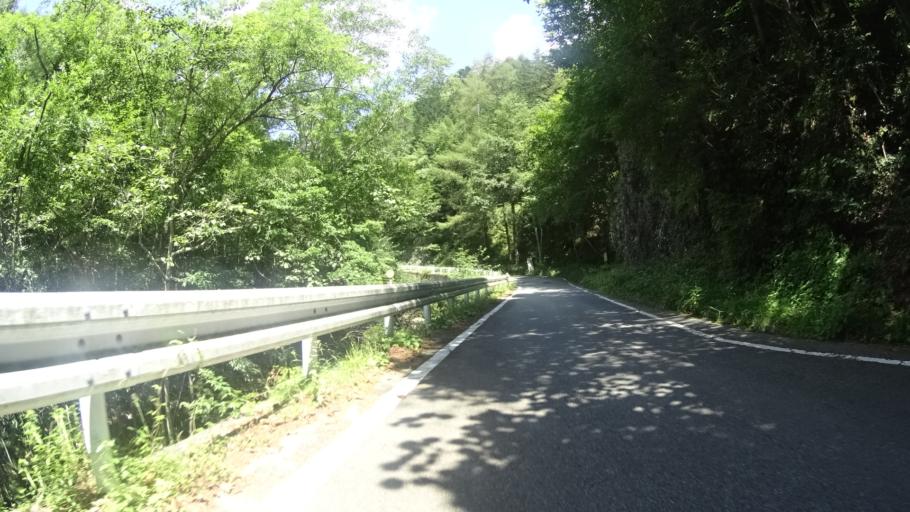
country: JP
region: Yamanashi
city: Enzan
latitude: 35.8171
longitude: 138.6542
